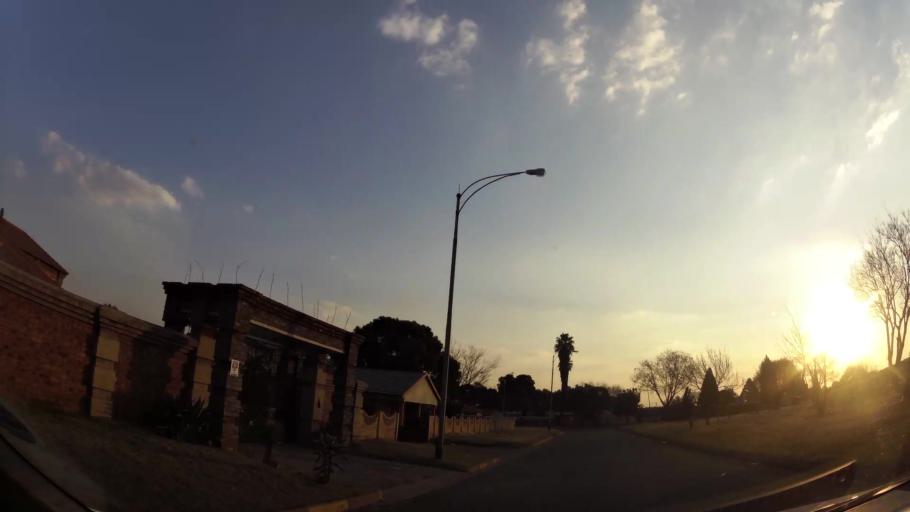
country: ZA
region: Gauteng
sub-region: Ekurhuleni Metropolitan Municipality
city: Springs
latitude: -26.2658
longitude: 28.4042
